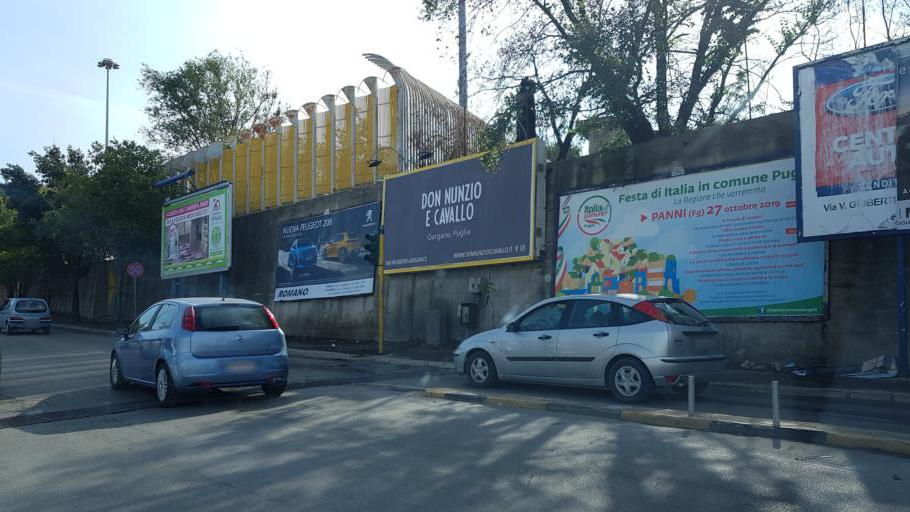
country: IT
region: Apulia
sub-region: Provincia di Foggia
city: Foggia
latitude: 41.4623
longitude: 15.5631
